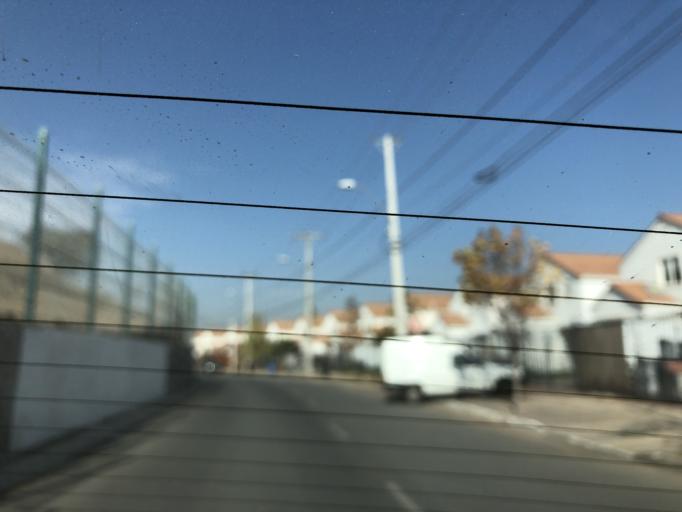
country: CL
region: Santiago Metropolitan
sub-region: Provincia de Cordillera
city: Puente Alto
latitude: -33.5740
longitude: -70.5397
